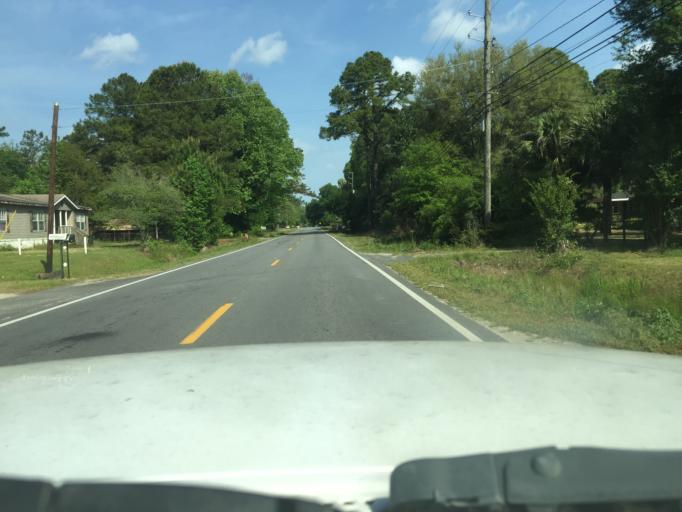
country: US
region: Georgia
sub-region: Chatham County
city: Georgetown
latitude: 32.0262
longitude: -81.2176
